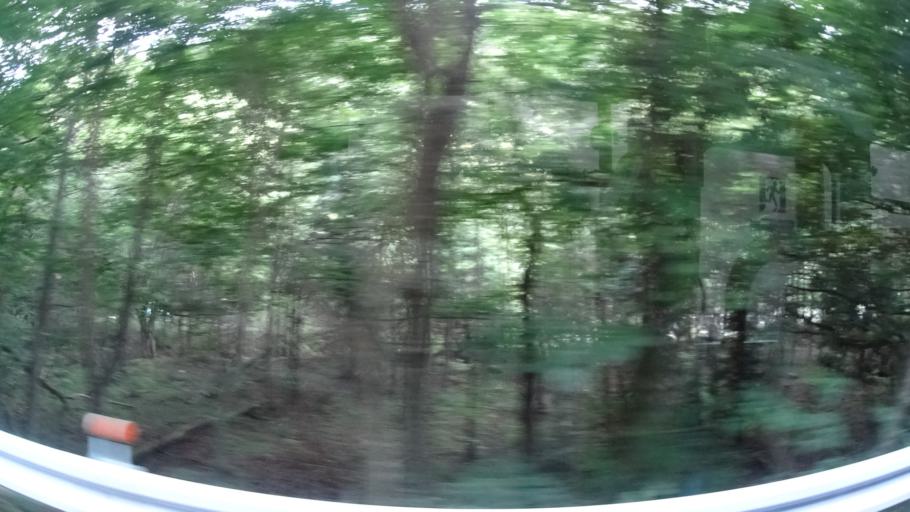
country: JP
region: Tochigi
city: Nikko
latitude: 36.6927
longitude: 139.5007
